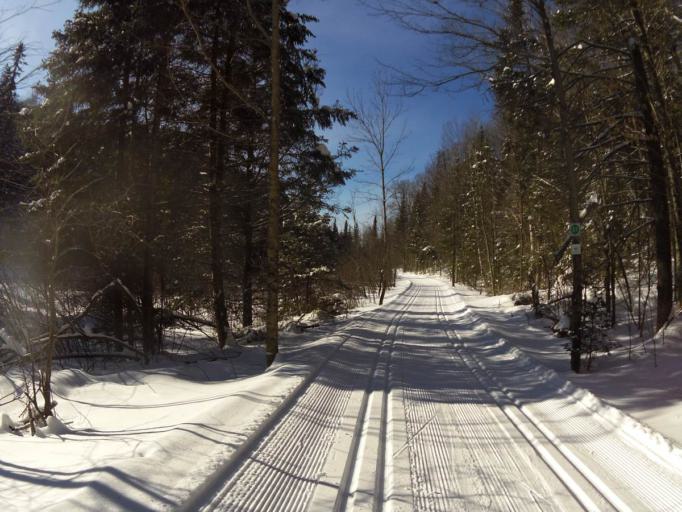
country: CA
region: Quebec
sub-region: Outaouais
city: Wakefield
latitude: 45.6234
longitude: -75.9936
